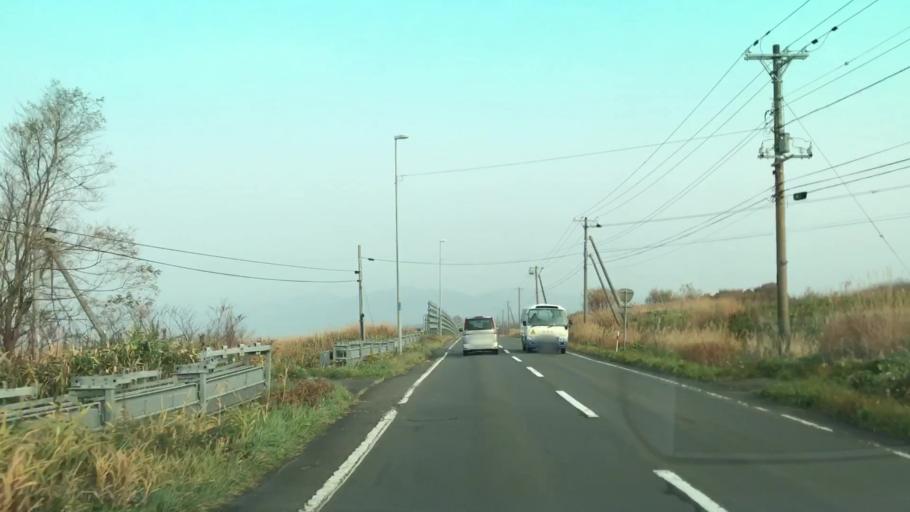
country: JP
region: Hokkaido
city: Ishikari
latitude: 43.3440
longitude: 141.4236
